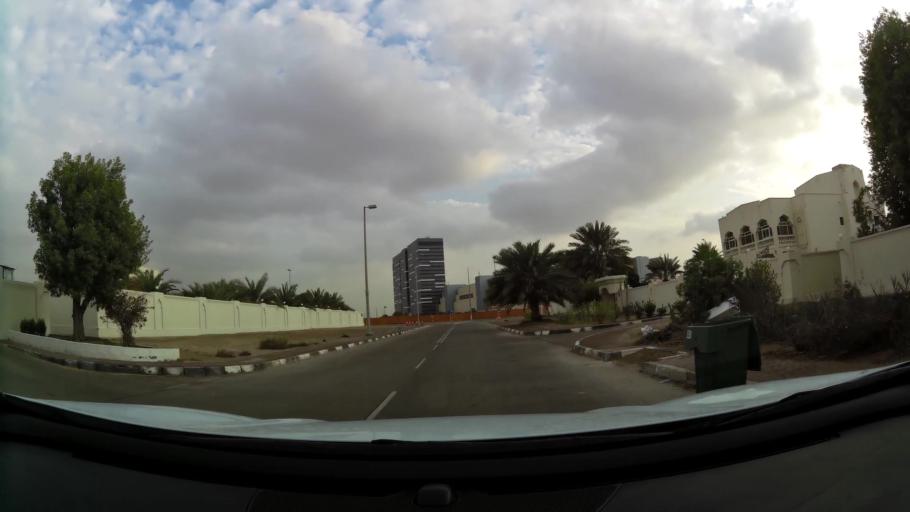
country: AE
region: Abu Dhabi
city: Abu Dhabi
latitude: 24.3795
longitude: 54.5309
